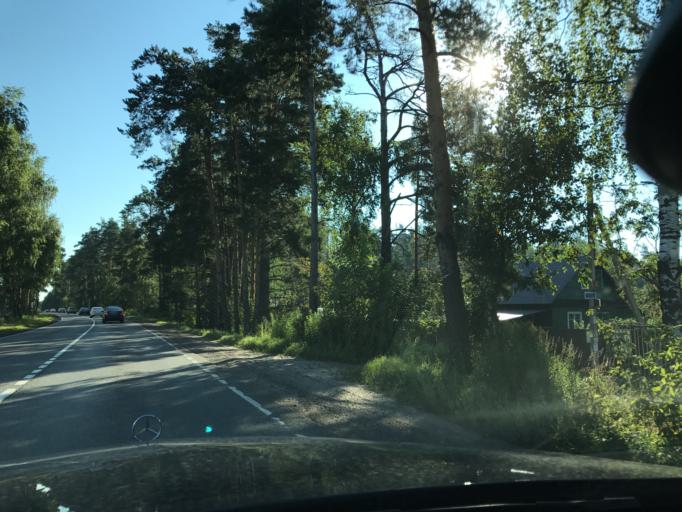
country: RU
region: Moskovskaya
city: Bakhchivandzhi
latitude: 55.8492
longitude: 38.1130
